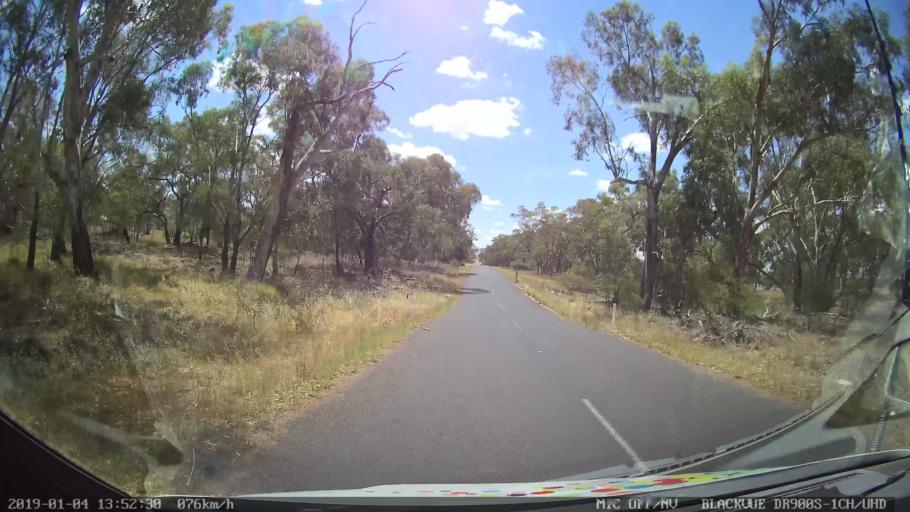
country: AU
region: New South Wales
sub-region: Dubbo Municipality
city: Dubbo
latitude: -32.3936
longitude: 148.5715
